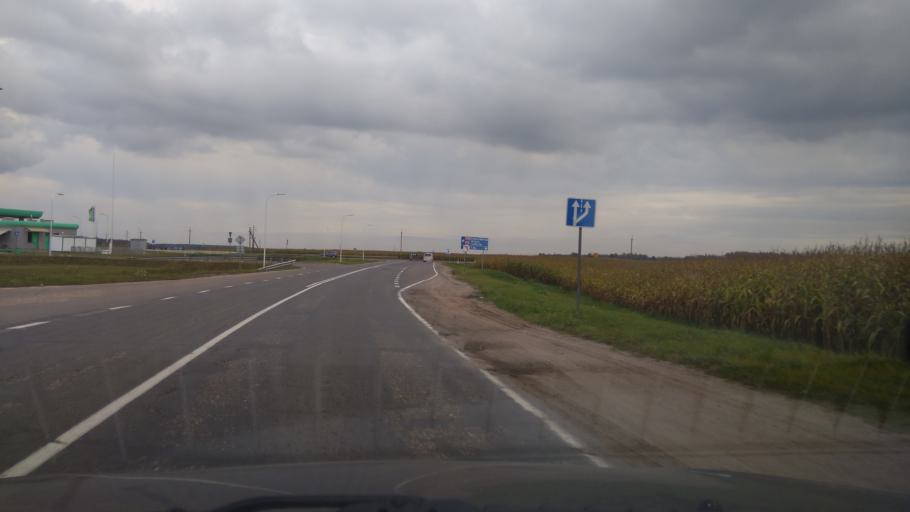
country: BY
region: Minsk
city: Dukora
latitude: 53.6557
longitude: 27.9419
